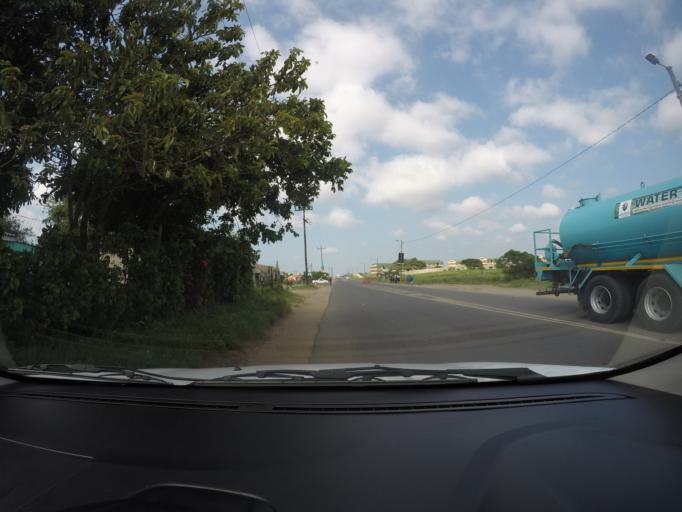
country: ZA
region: KwaZulu-Natal
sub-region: uThungulu District Municipality
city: eSikhawini
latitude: -28.8813
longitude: 31.9066
